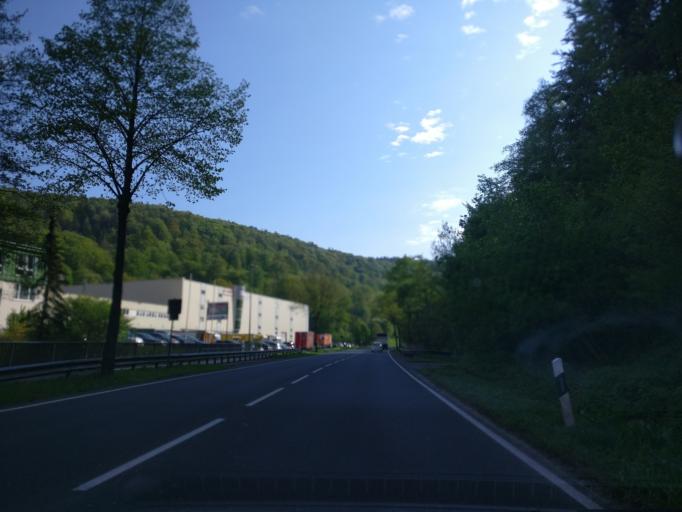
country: DE
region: Lower Saxony
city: Hannoversch Munden
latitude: 51.4475
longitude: 9.6685
